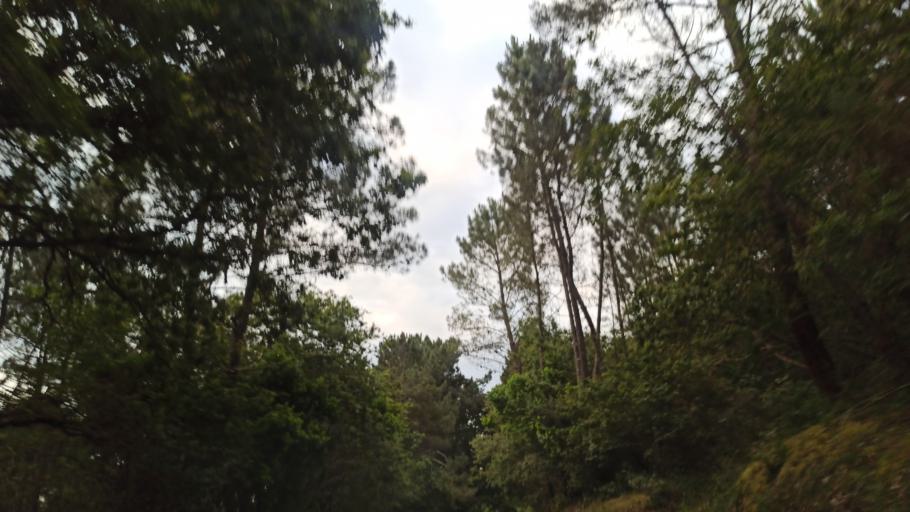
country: ES
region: Galicia
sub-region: Provincia da Coruna
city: Santiso
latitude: 42.8272
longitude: -8.1293
